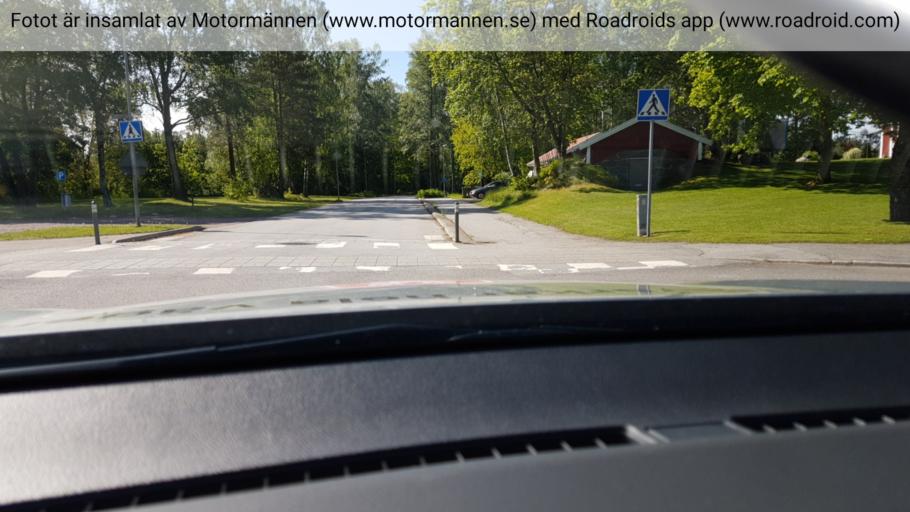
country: SE
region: Vaestra Goetaland
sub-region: Tibro Kommun
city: Tibro
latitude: 58.4260
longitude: 14.1459
